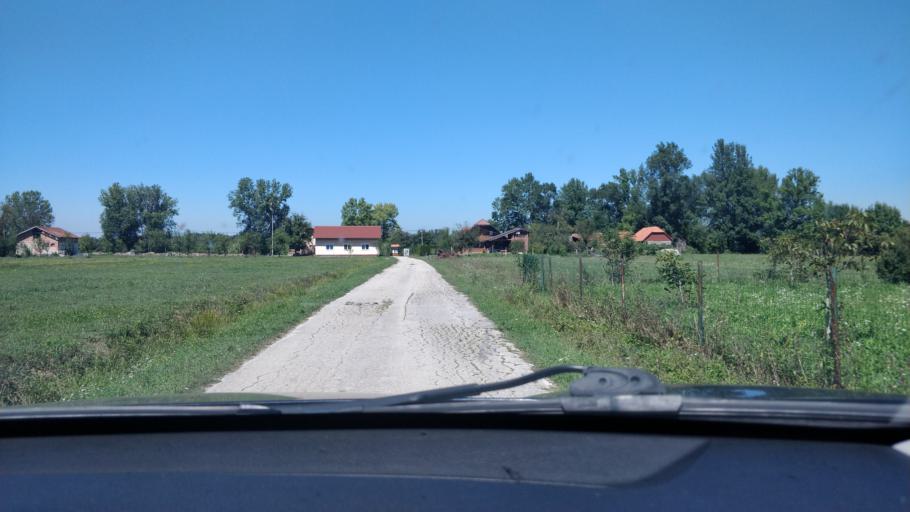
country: HR
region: Karlovacka
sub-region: Grad Karlovac
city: Karlovac
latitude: 45.4772
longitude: 15.6637
